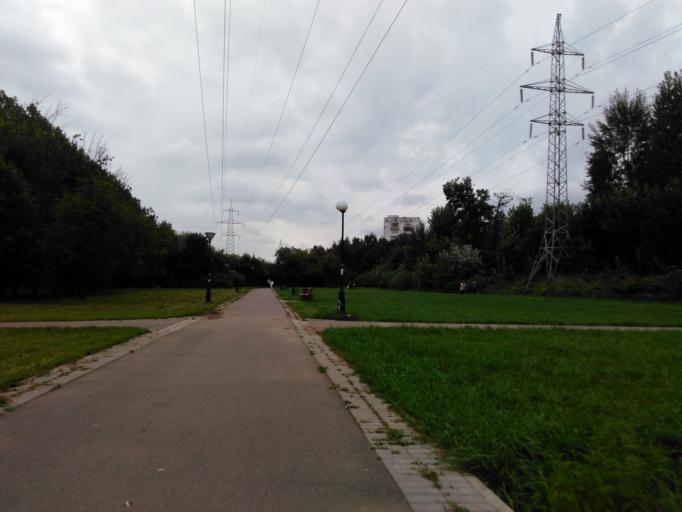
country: RU
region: Moscow
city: Zyuzino
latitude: 55.6472
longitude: 37.5858
